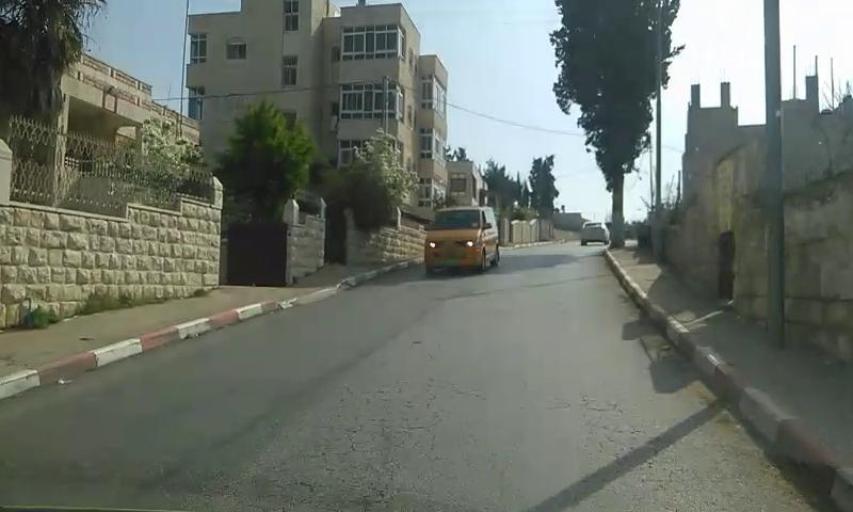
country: PS
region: West Bank
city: `Ayn Yabrud
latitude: 31.9540
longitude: 35.2499
